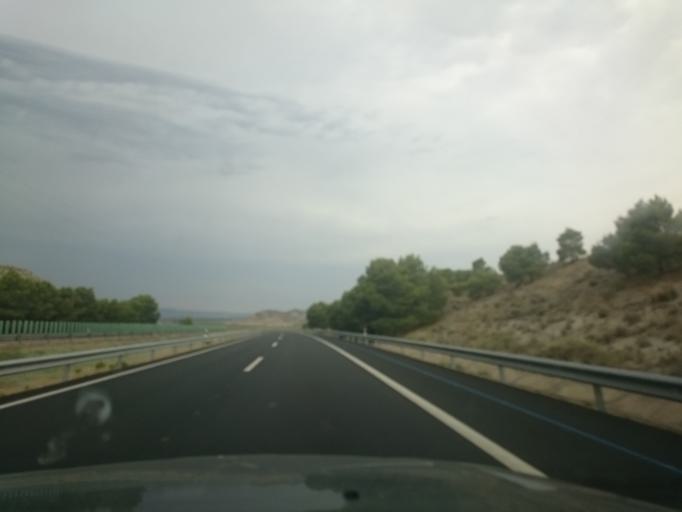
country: ES
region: Aragon
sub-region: Provincia de Zaragoza
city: Pina de Ebro
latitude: 41.5449
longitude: -0.5438
